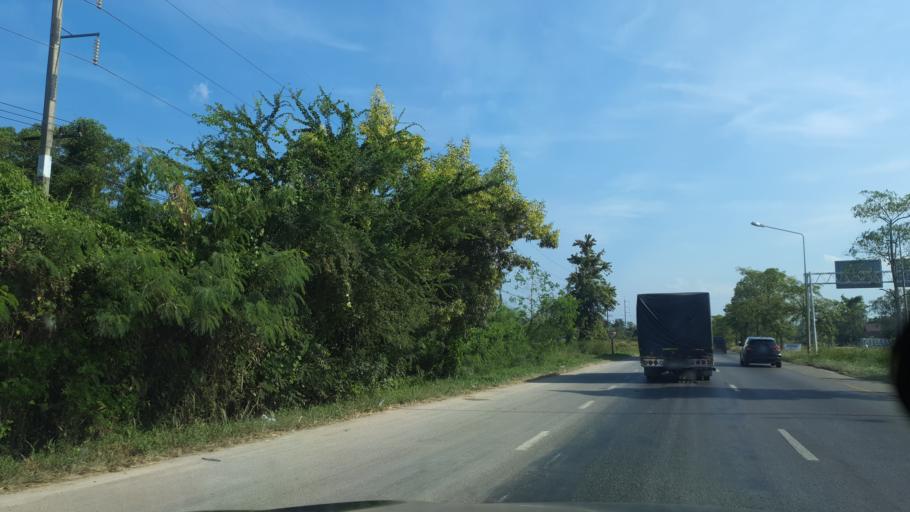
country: TH
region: Surat Thani
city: Phunphin
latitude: 9.0953
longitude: 99.1646
